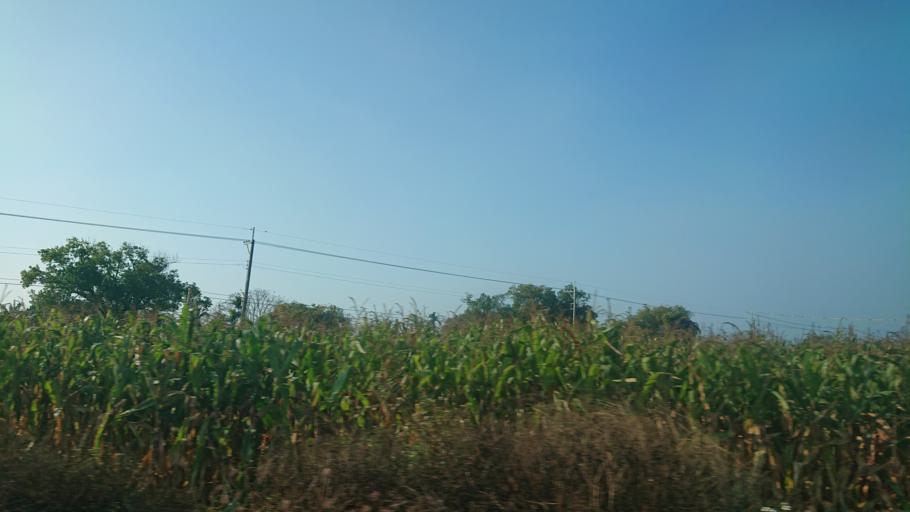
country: TW
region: Taiwan
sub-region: Tainan
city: Tainan
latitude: 23.1243
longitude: 120.2243
